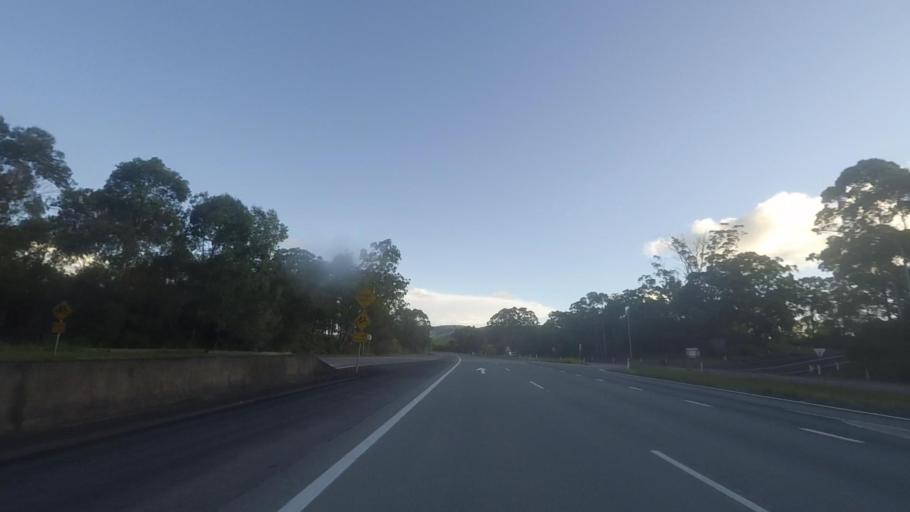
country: AU
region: New South Wales
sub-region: Great Lakes
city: Nabiac
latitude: -32.2519
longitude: 152.3233
